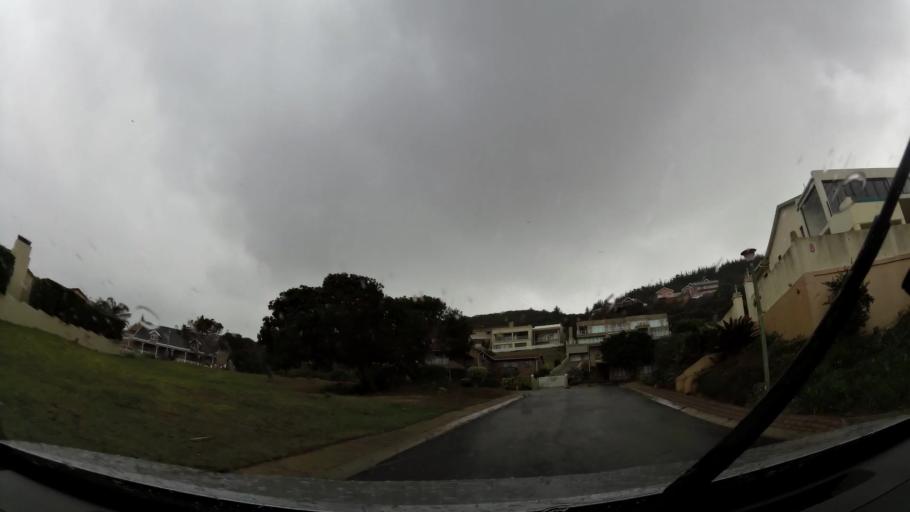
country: ZA
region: Western Cape
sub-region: Eden District Municipality
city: George
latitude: -34.0481
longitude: 22.2893
